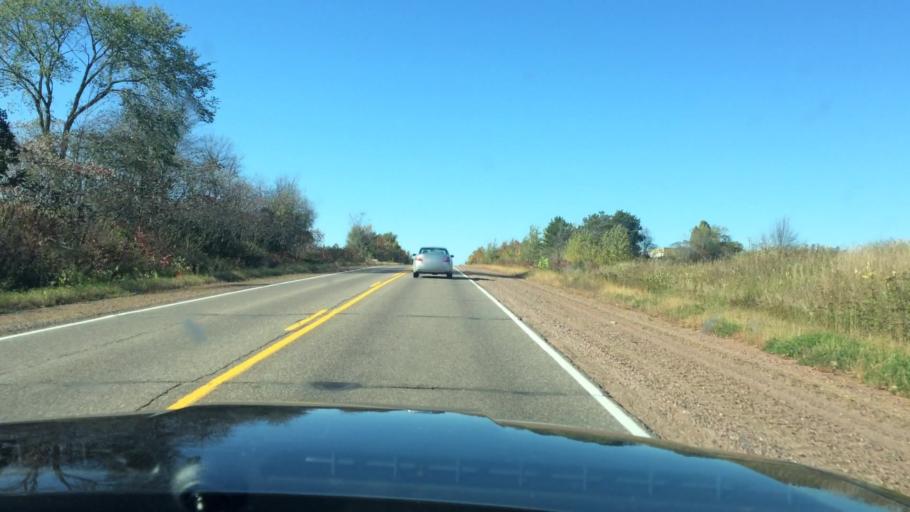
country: US
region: Wisconsin
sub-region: Marathon County
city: Wausau
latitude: 45.0053
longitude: -89.6714
